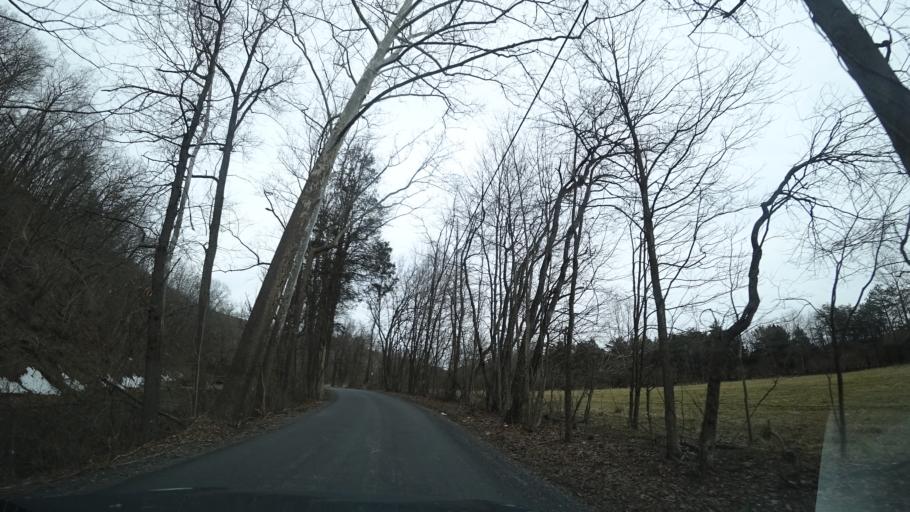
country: US
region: Virginia
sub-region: Shenandoah County
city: Woodstock
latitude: 39.0664
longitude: -78.6304
